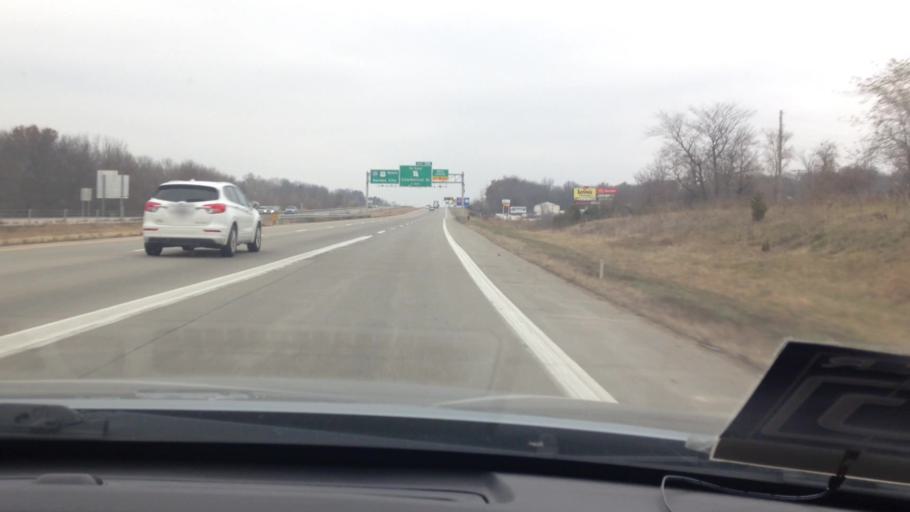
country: US
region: Missouri
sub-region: Cass County
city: Harrisonville
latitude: 38.6199
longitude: -94.3486
